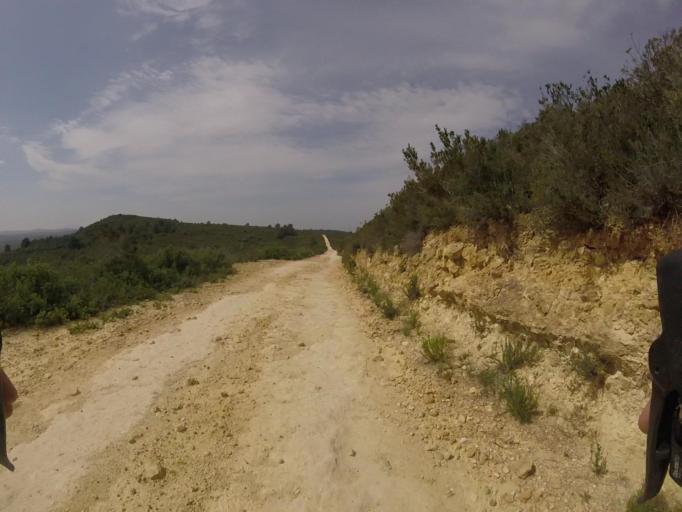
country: ES
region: Valencia
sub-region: Provincia de Castello
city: Cuevas de Vinroma
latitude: 40.2618
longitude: 0.1130
